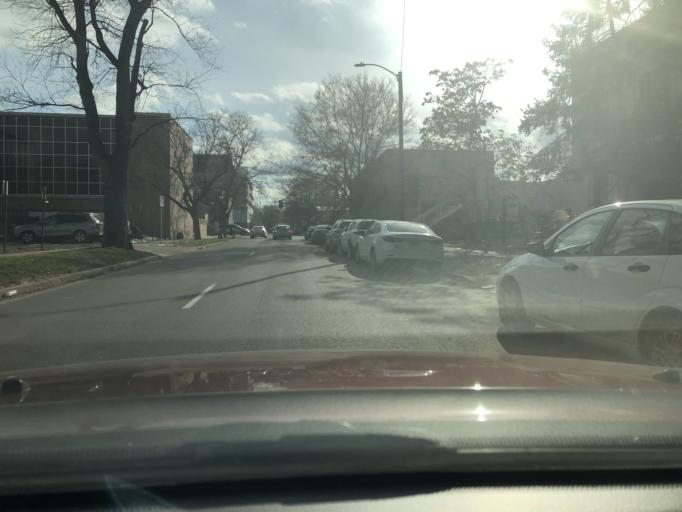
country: US
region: Colorado
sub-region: Denver County
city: Denver
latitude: 39.7408
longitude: -104.9788
